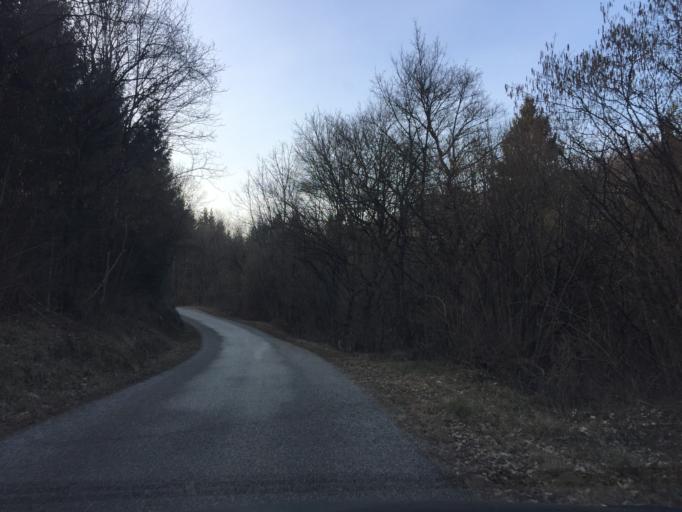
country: SI
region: Kanal
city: Kanal
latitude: 46.0611
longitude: 13.6669
